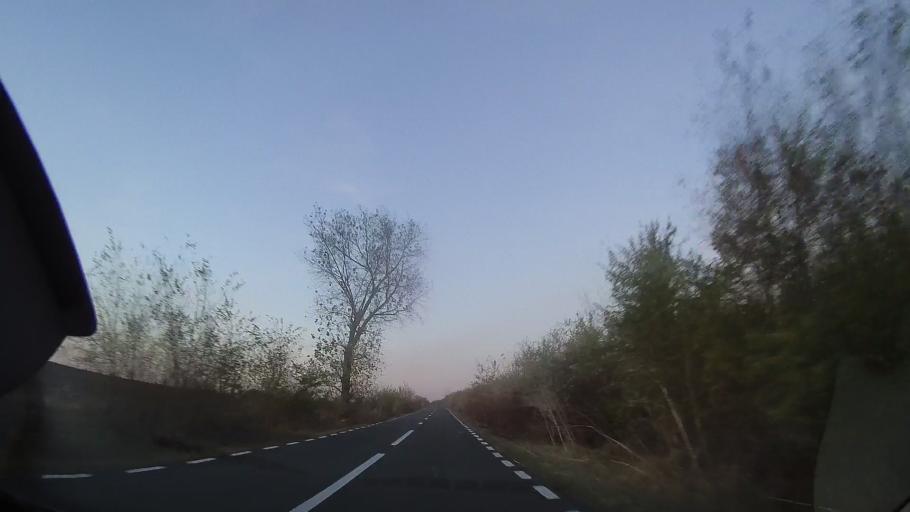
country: RO
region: Constanta
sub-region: Comuna Cobadin
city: Cobadin
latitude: 44.0319
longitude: 28.2608
